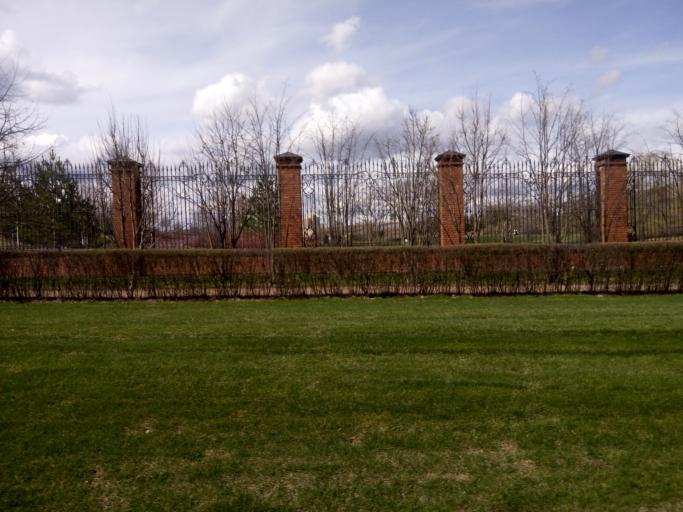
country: RU
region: Moskovskaya
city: Marfino
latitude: 55.6926
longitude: 37.3814
